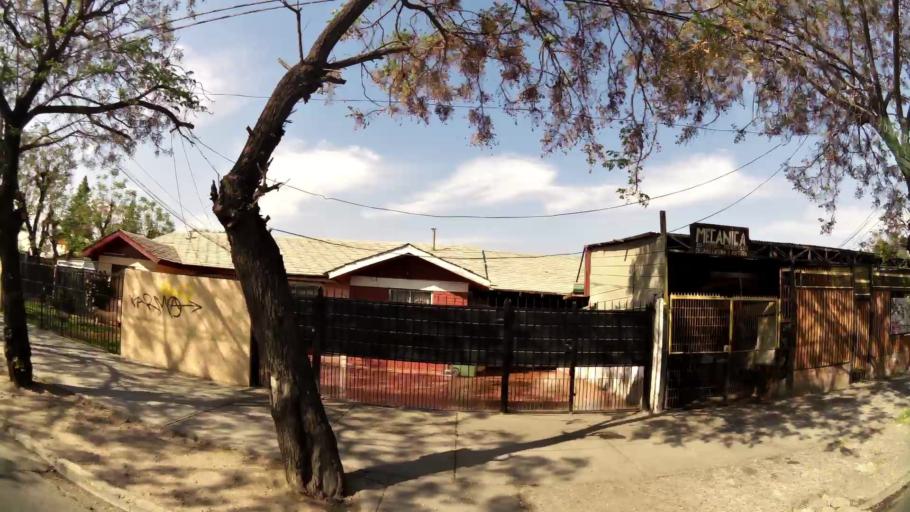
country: CL
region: Santiago Metropolitan
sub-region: Provincia de Santiago
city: La Pintana
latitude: -33.5472
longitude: -70.5889
